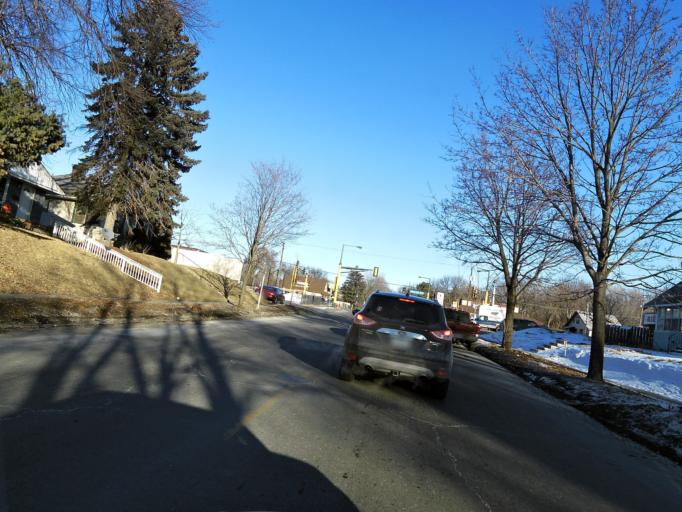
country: US
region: Minnesota
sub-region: Ramsey County
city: Maplewood
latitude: 44.9630
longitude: -93.0264
